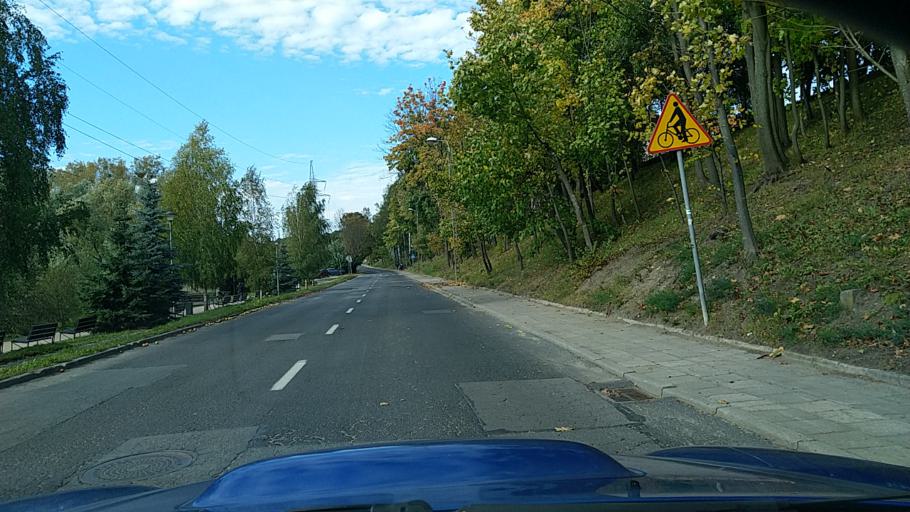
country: PL
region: Warmian-Masurian Voivodeship
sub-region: Olsztyn
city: Kortowo
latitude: 53.7791
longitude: 20.4651
